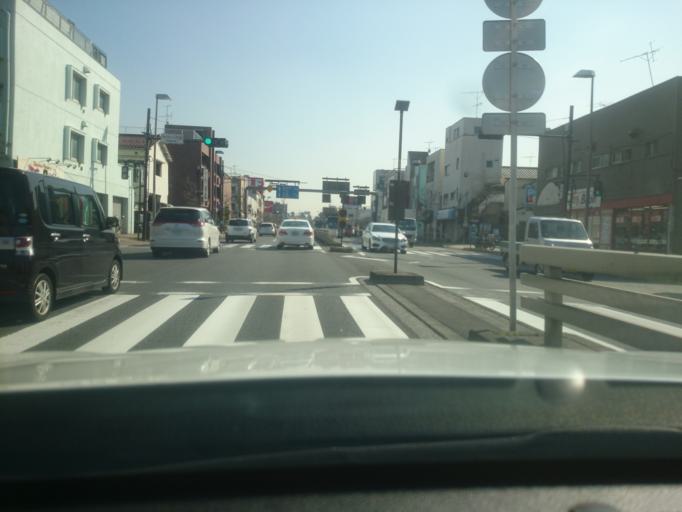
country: JP
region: Tokyo
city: Musashino
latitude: 35.7169
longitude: 139.6143
